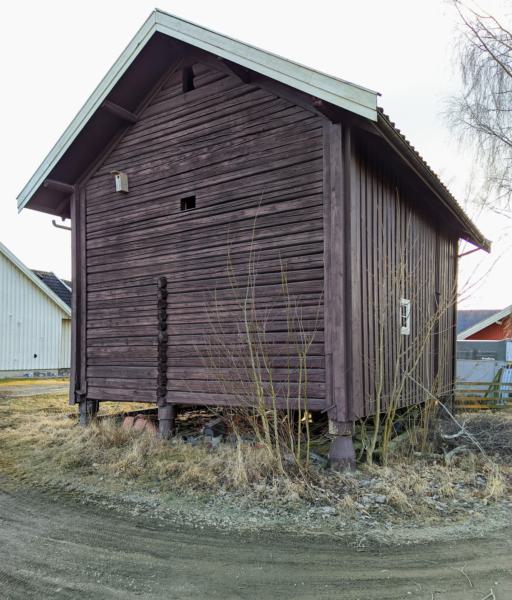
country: NO
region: Akershus
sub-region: Gjerdrum
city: Ask
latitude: 60.1449
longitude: 11.0516
